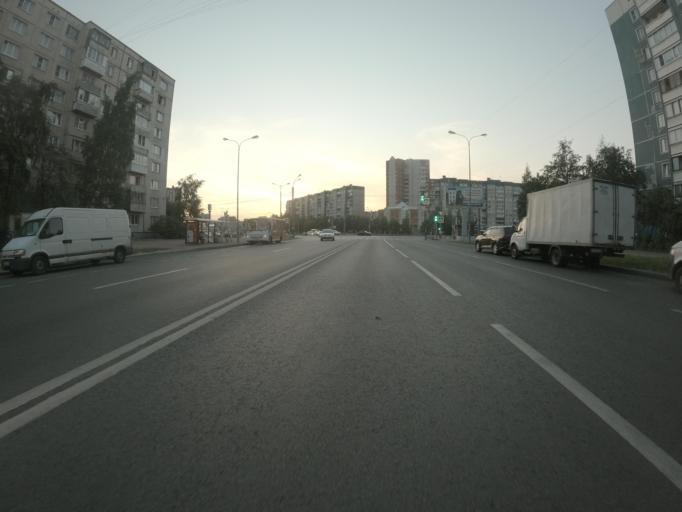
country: RU
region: St.-Petersburg
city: Krasnogvargeisky
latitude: 59.9158
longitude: 30.4574
